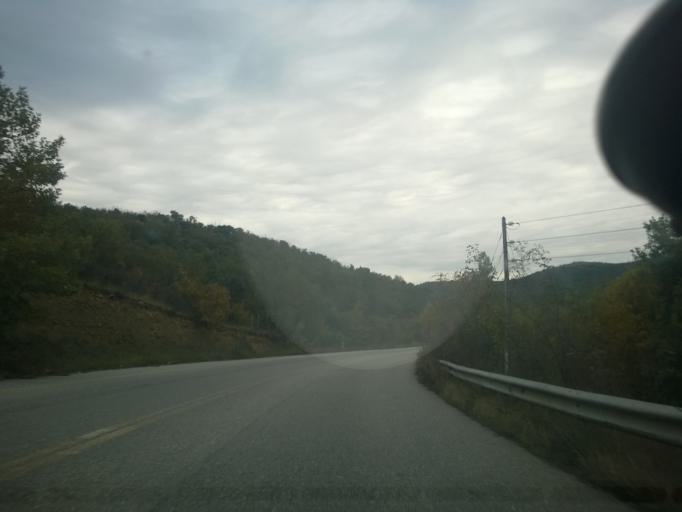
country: GR
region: Central Macedonia
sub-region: Nomos Pellis
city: Profitis Ilias
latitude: 40.8399
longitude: 22.1171
